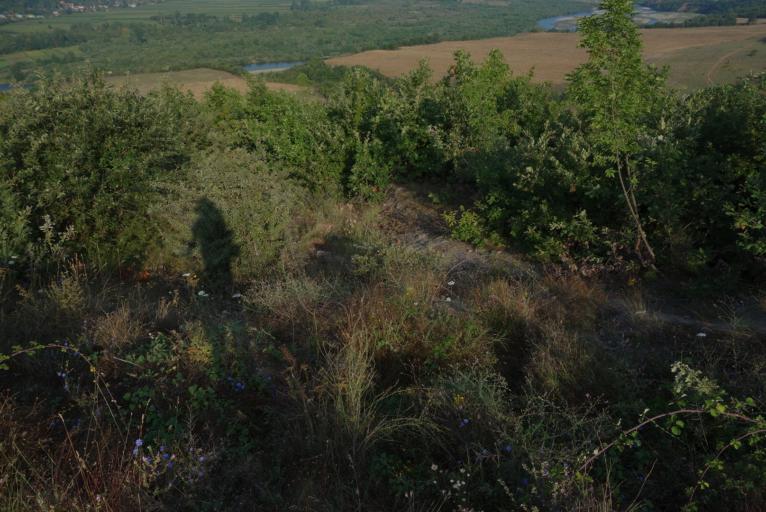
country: AL
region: Diber
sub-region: Rrethi i Dibres
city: Tomin
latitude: 41.6564
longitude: 20.3956
